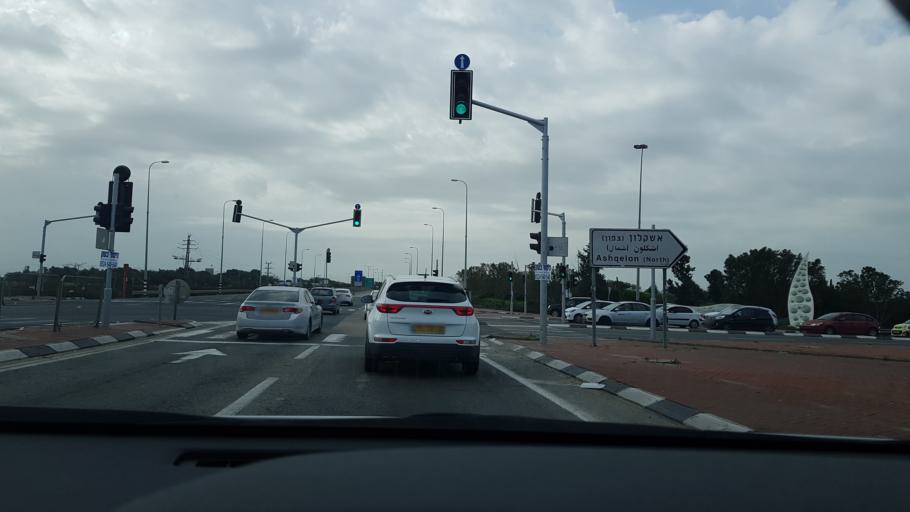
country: IL
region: Southern District
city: Ashqelon
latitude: 31.6807
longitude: 34.6096
